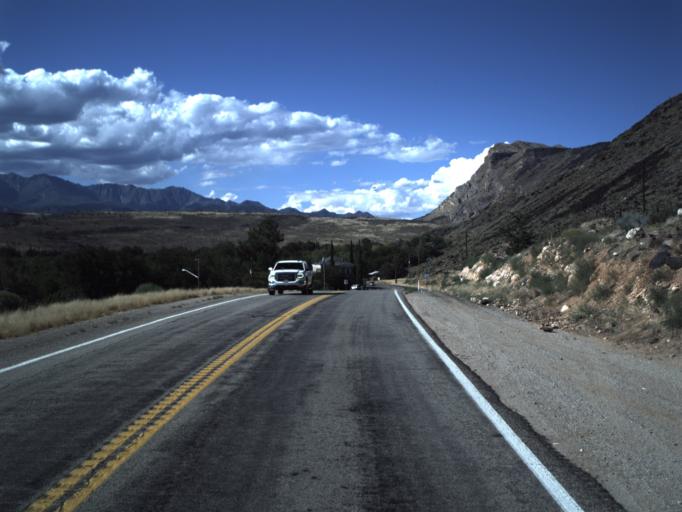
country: US
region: Utah
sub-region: Washington County
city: Toquerville
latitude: 37.2463
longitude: -113.2838
